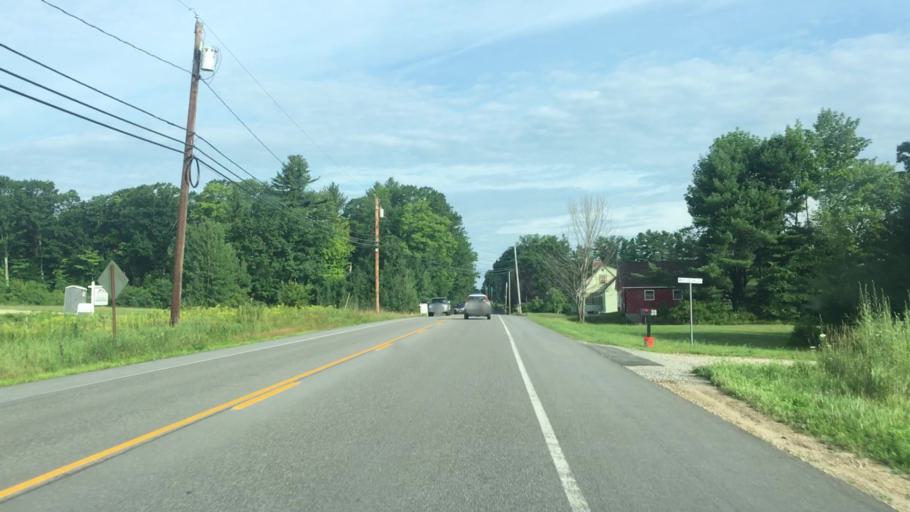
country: US
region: Maine
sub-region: Cumberland County
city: Gorham
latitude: 43.6878
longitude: -70.4843
